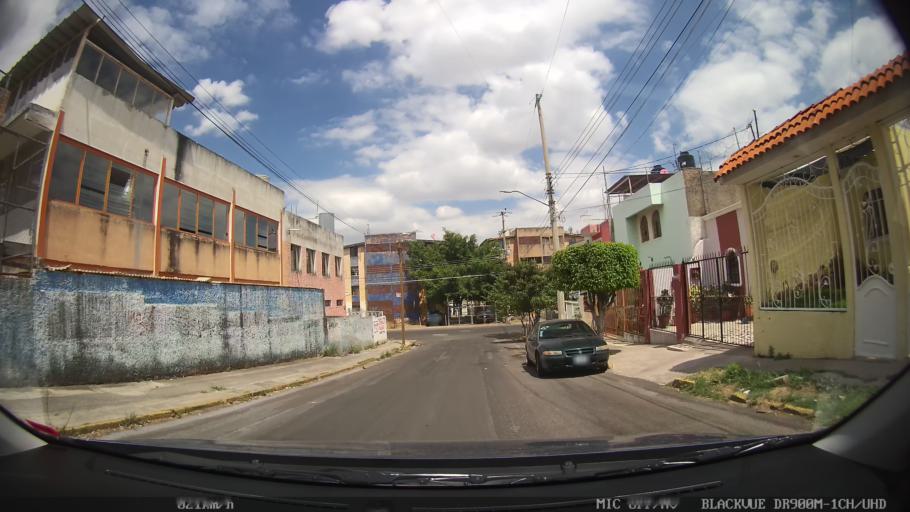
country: MX
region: Jalisco
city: Tonala
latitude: 20.6282
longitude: -103.2538
